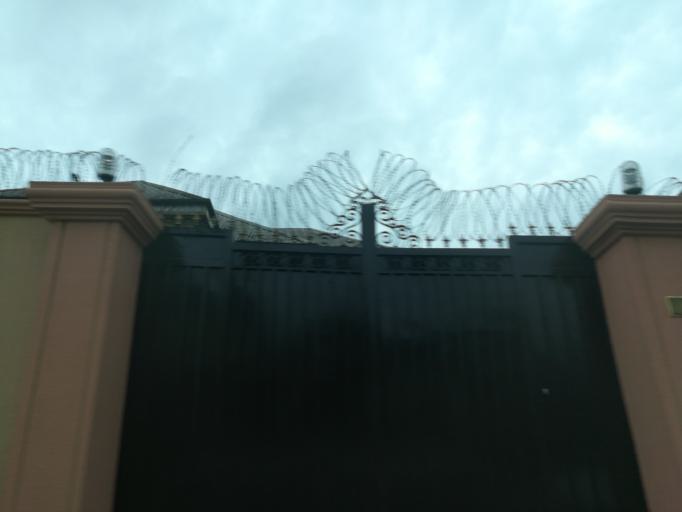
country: NG
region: Rivers
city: Port Harcourt
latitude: 4.8341
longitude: 7.0183
